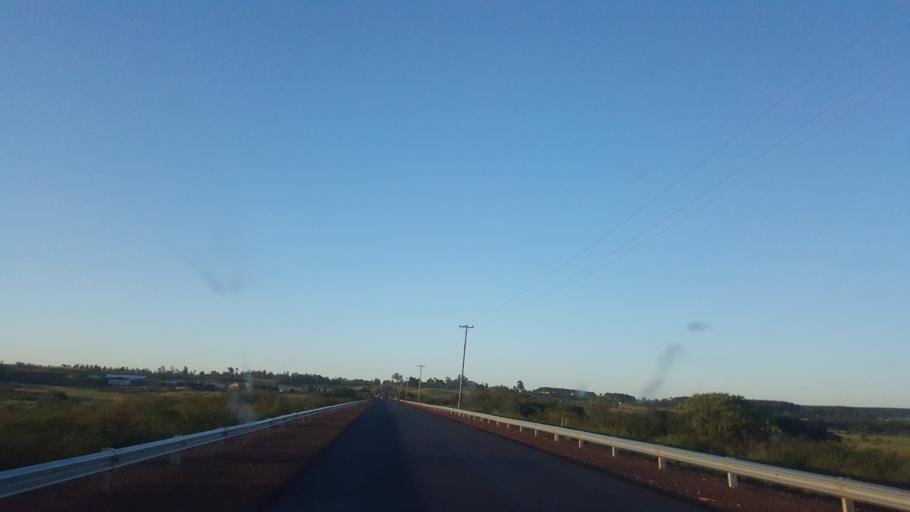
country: AR
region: Corrientes
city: Santo Tome
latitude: -28.5343
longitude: -56.0522
